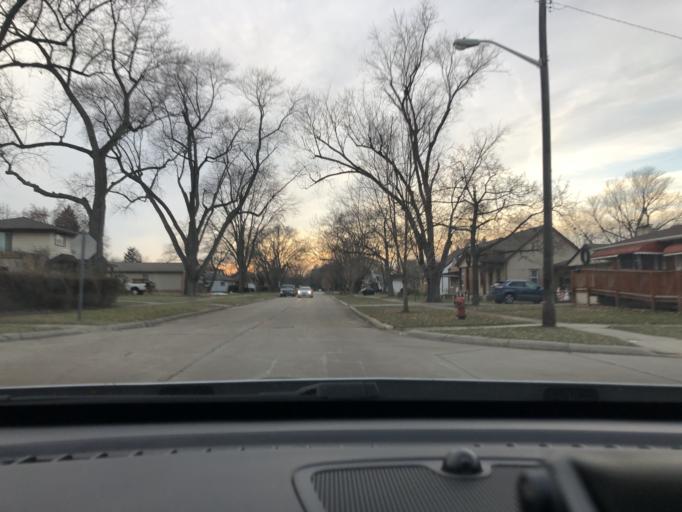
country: US
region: Michigan
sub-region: Wayne County
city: Allen Park
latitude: 42.2735
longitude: -83.2361
